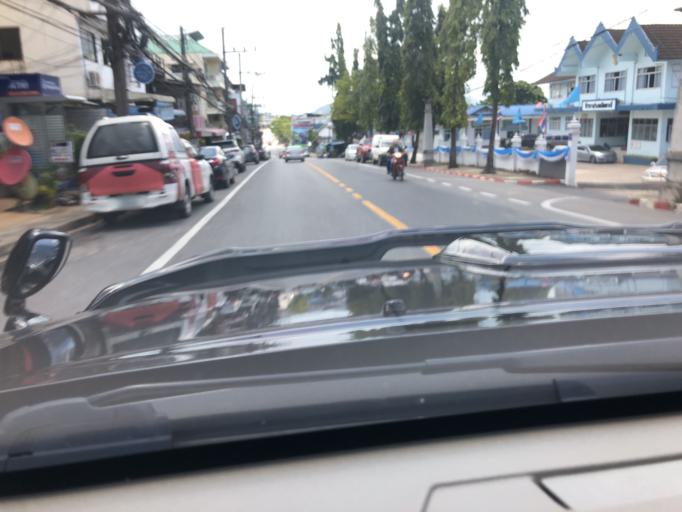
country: TH
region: Krabi
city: Krabi
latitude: 8.0611
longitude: 98.9184
